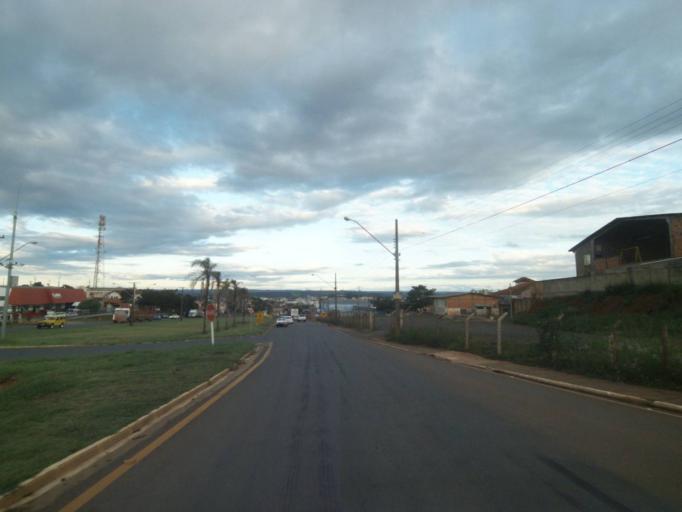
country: BR
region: Parana
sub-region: Telemaco Borba
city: Telemaco Borba
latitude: -24.3305
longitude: -50.6456
